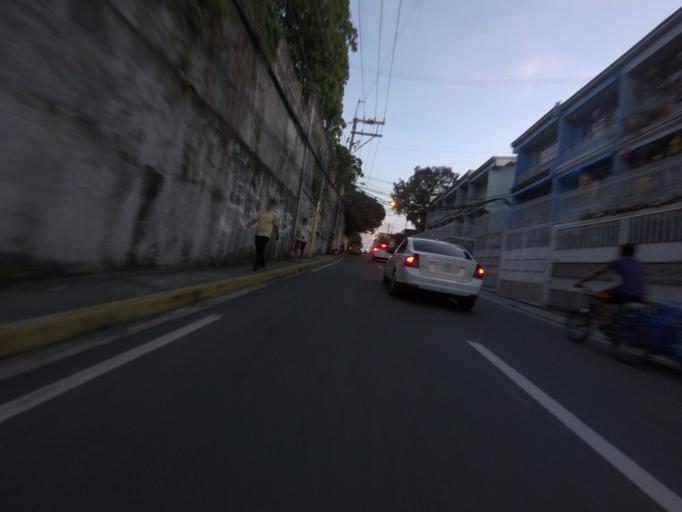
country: PH
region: Metro Manila
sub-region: Mandaluyong
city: Mandaluyong City
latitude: 14.5917
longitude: 121.0379
